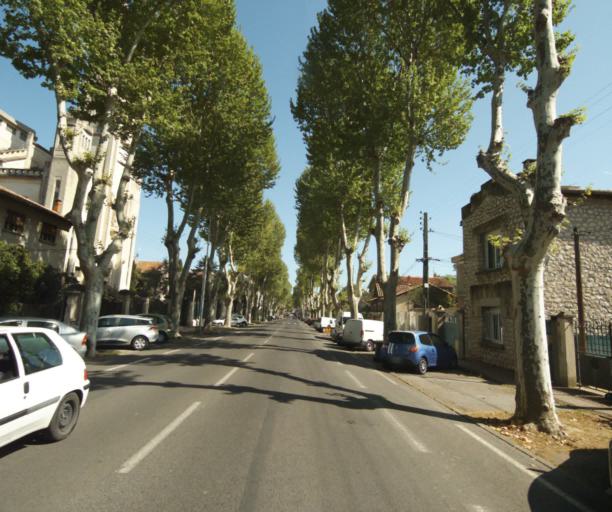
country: FR
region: Languedoc-Roussillon
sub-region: Departement de l'Herault
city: Montpellier
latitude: 43.6154
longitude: 3.8636
